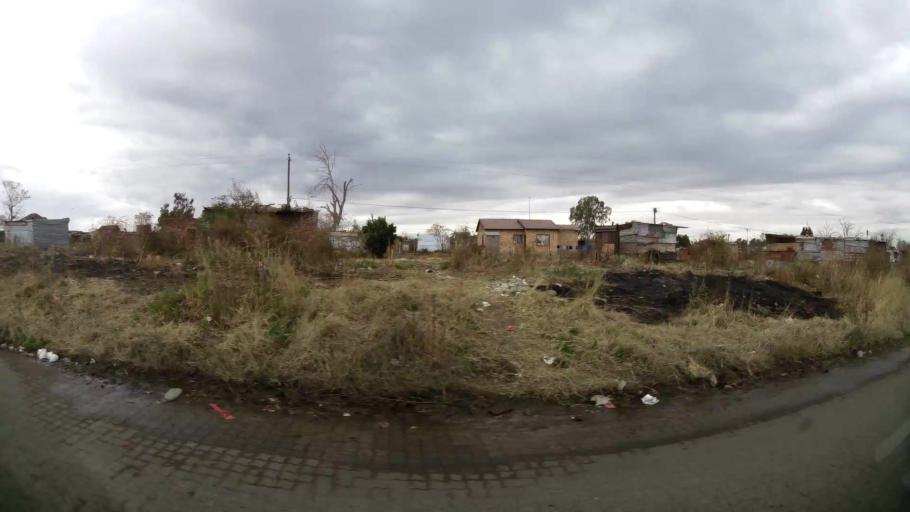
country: ZA
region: Orange Free State
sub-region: Fezile Dabi District Municipality
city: Kroonstad
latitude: -27.6509
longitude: 27.2216
